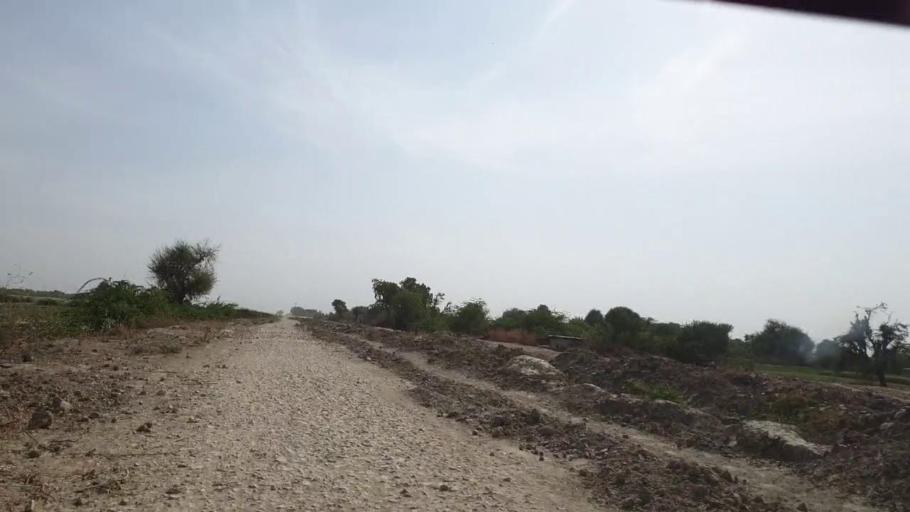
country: PK
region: Sindh
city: Nabisar
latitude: 25.0633
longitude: 69.5778
